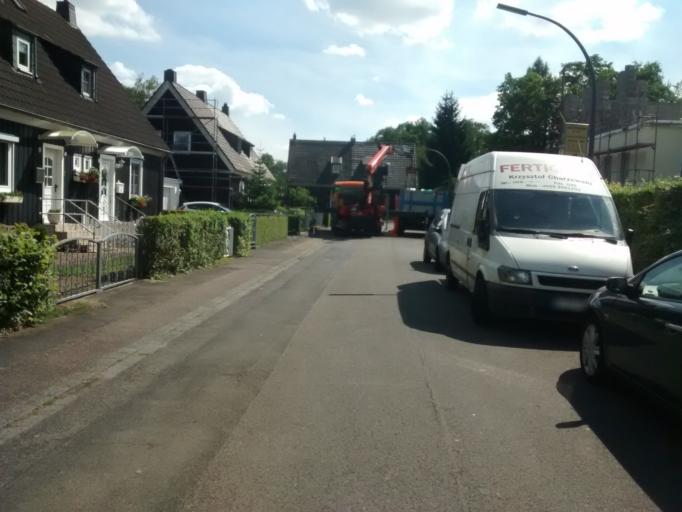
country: DE
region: North Rhine-Westphalia
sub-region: Regierungsbezirk Koln
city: Buchheim
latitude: 50.9885
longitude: 7.0415
